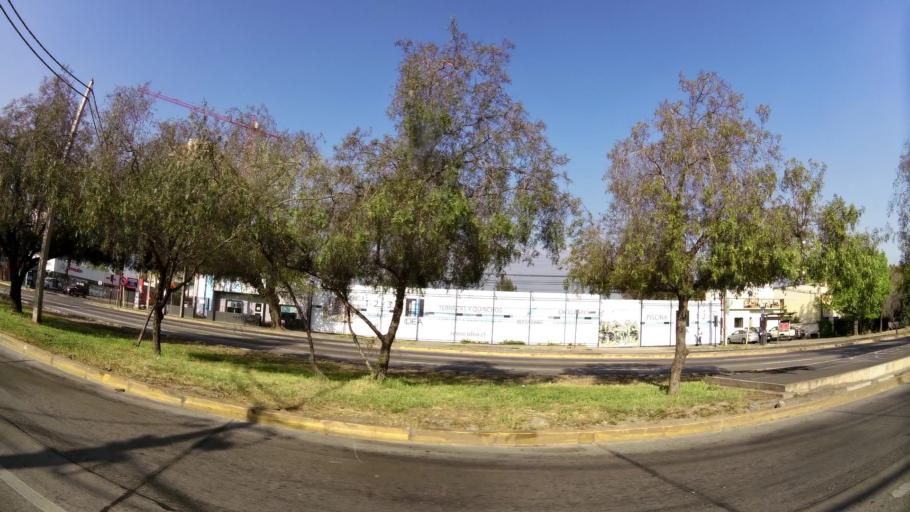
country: CL
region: Santiago Metropolitan
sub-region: Provincia de Santiago
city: Villa Presidente Frei, Nunoa, Santiago, Chile
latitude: -33.4559
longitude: -70.5715
